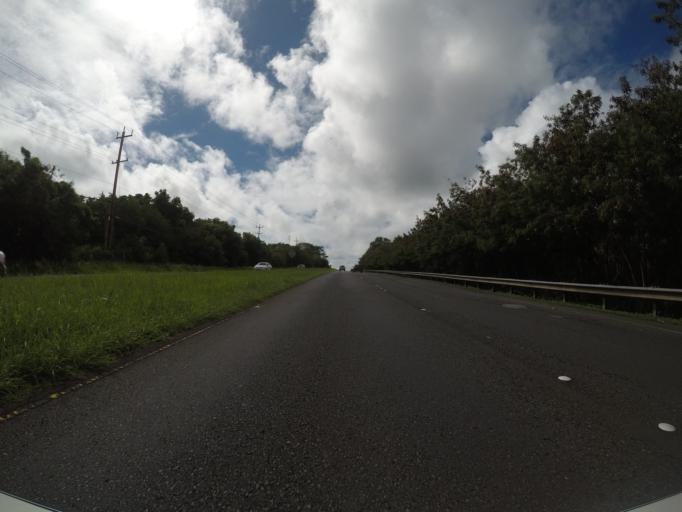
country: US
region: Hawaii
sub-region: Honolulu County
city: Maunawili
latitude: 21.3752
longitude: -157.7469
